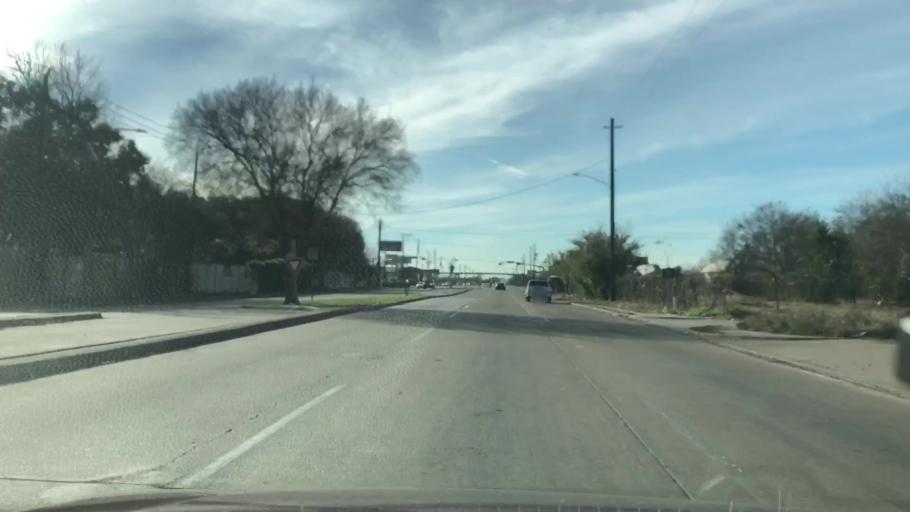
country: US
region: Texas
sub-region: Harris County
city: Bellaire
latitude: 29.6594
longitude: -95.4642
